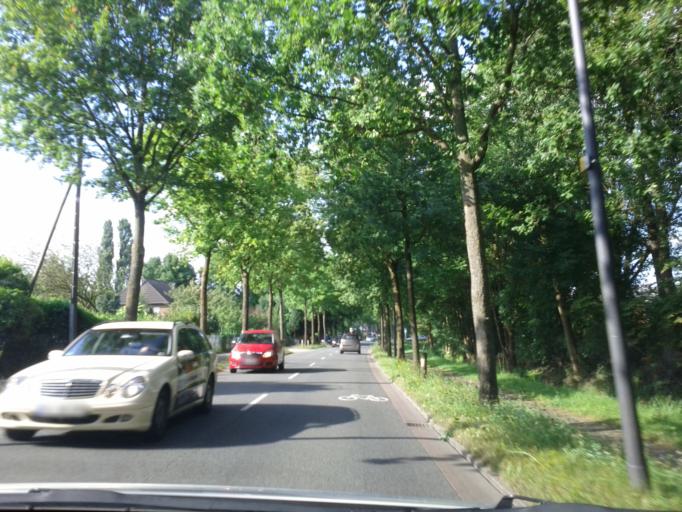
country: DE
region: Bremen
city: Bremen
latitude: 53.1064
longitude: 8.8173
